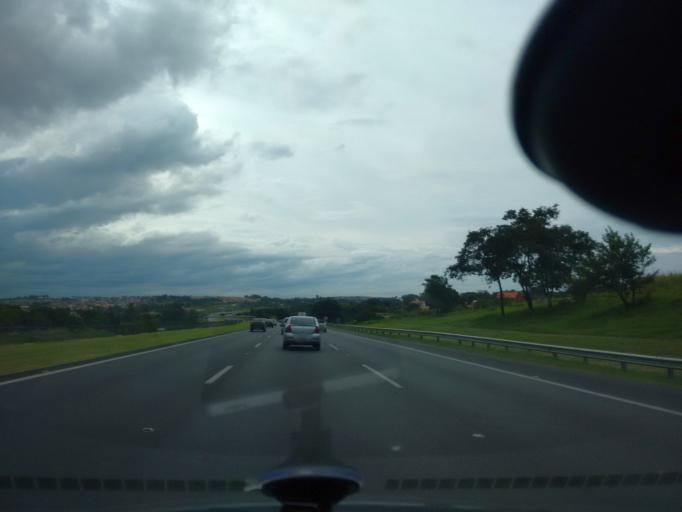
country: BR
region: Sao Paulo
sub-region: Campinas
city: Campinas
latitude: -22.9716
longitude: -47.1158
